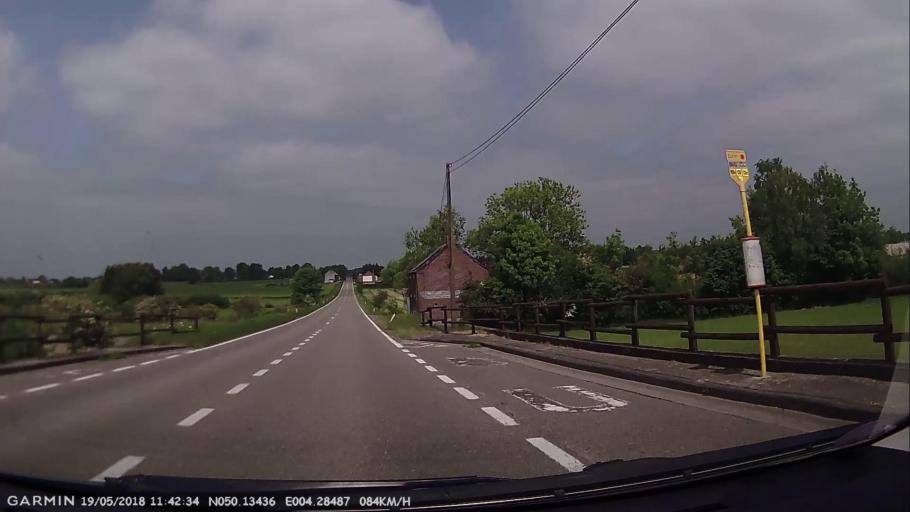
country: BE
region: Wallonia
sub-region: Province du Hainaut
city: Froidchapelle
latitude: 50.1345
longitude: 4.2848
